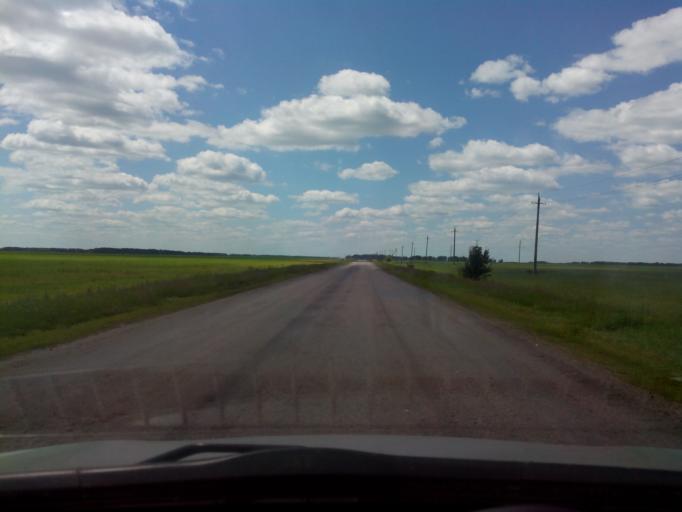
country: RU
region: Voronezj
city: Gribanovskiy
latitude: 51.6226
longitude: 41.8803
